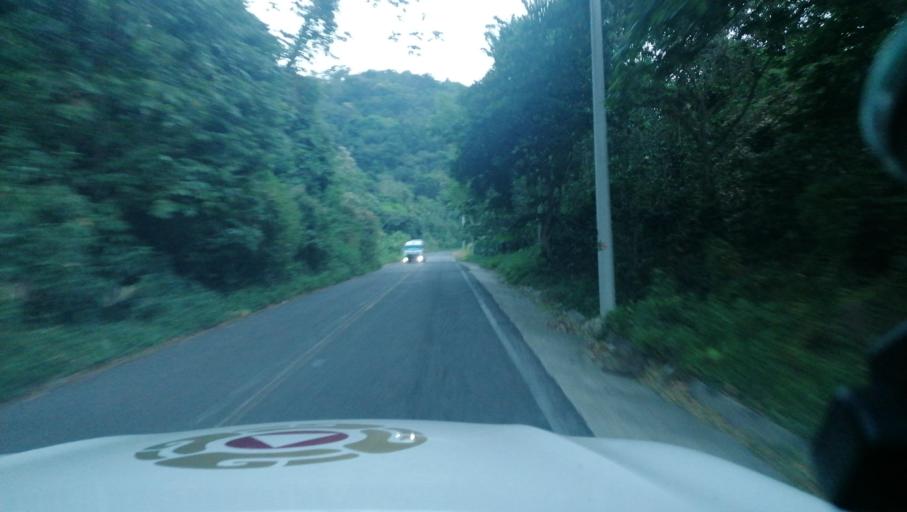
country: MX
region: Chiapas
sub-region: Cacahoatan
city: Benito Juarez
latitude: 15.0429
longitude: -92.2442
